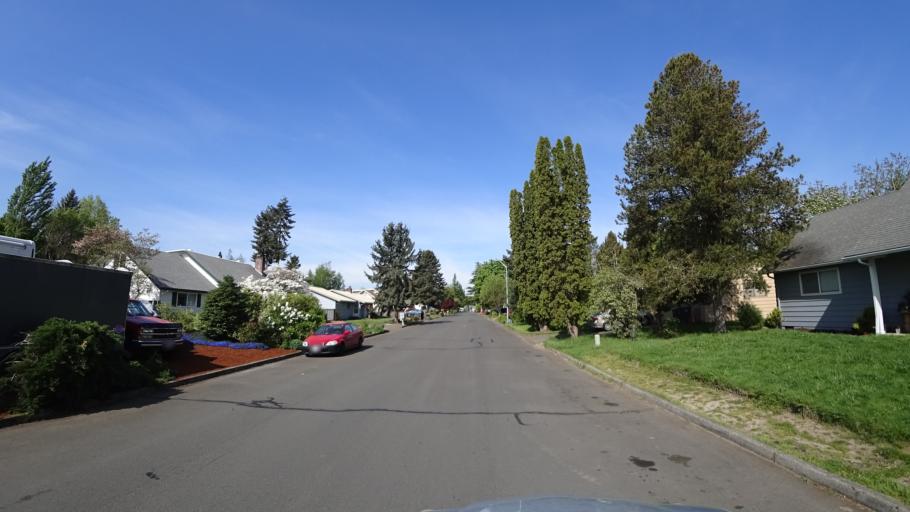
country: US
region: Oregon
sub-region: Washington County
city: Hillsboro
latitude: 45.5225
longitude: -122.9500
